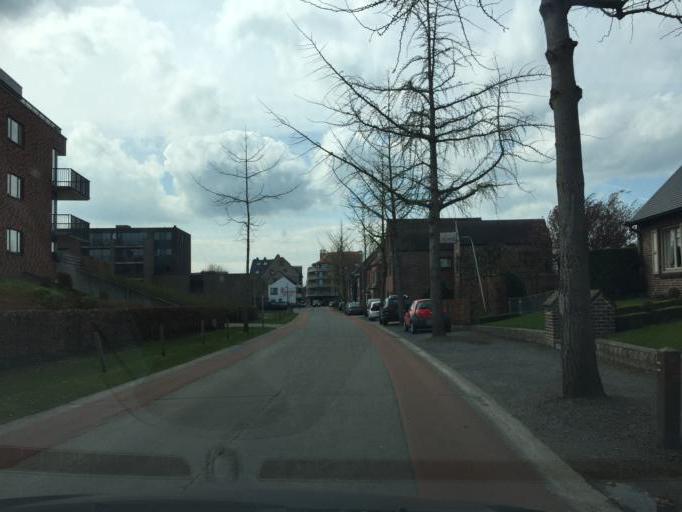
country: BE
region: Flanders
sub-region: Provincie Oost-Vlaanderen
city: Aalter
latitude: 51.0882
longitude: 3.4509
